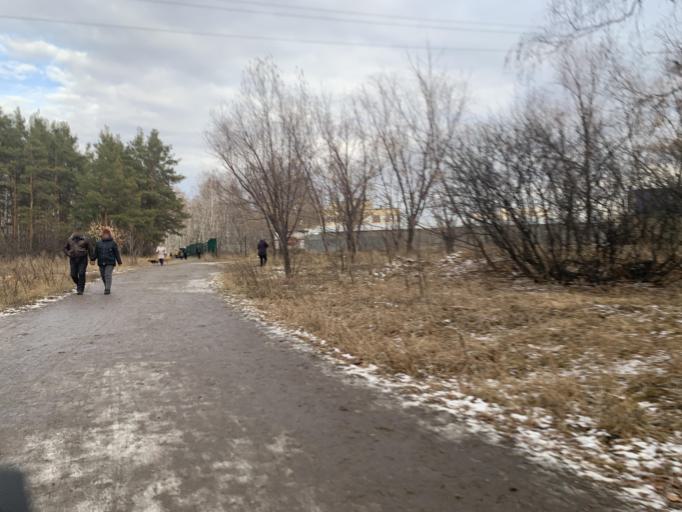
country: RU
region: Chelyabinsk
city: Roshchino
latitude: 55.1987
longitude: 61.3005
